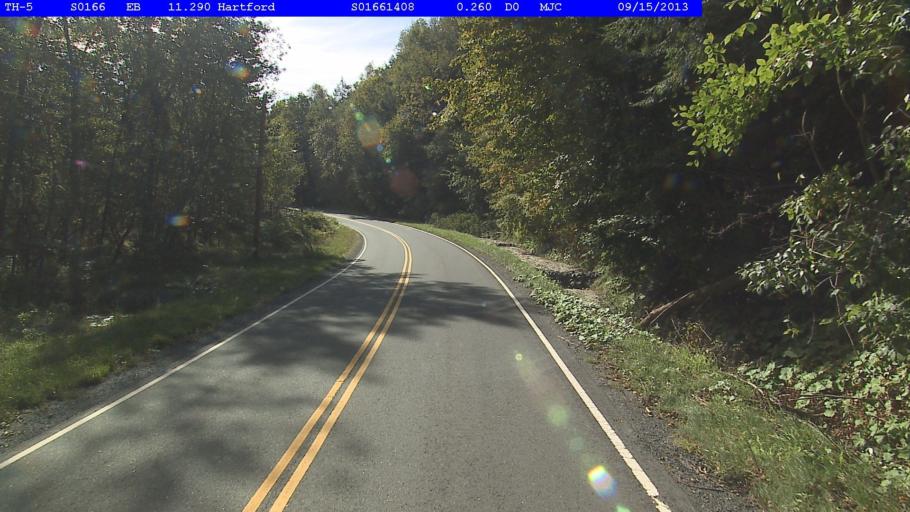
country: US
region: Vermont
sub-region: Windsor County
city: Wilder
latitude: 43.7194
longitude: -72.4226
